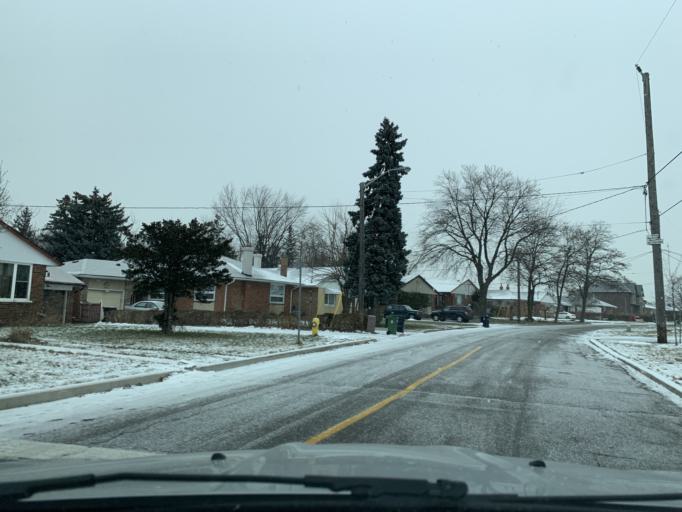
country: CA
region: Ontario
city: Concord
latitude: 43.7337
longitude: -79.4939
